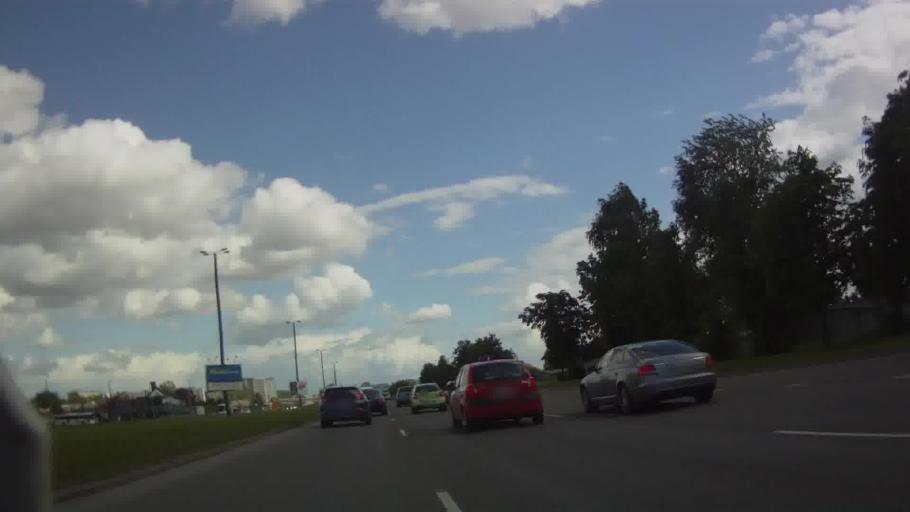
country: LV
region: Riga
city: Riga
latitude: 56.9287
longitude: 24.1548
